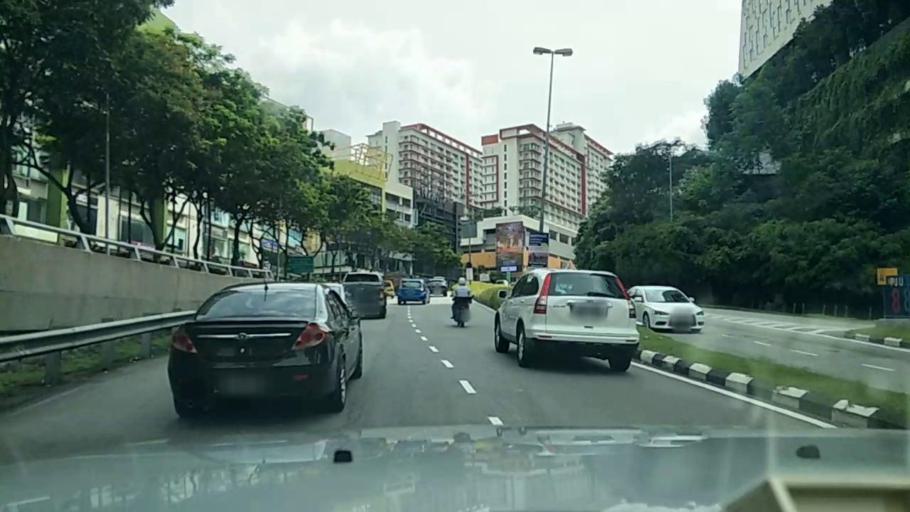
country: MY
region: Selangor
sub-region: Petaling
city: Petaling Jaya
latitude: 3.1653
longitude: 101.6133
